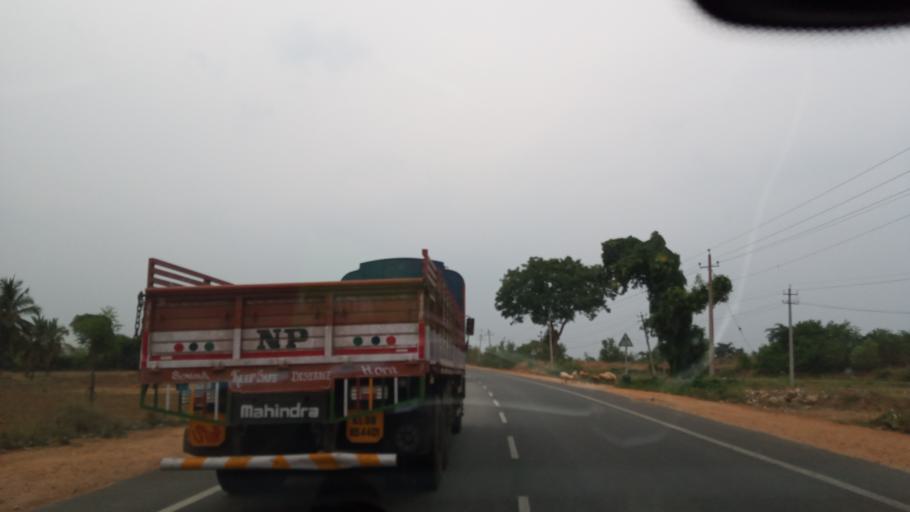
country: IN
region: Karnataka
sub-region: Mandya
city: Nagamangala
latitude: 12.7909
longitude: 76.7509
